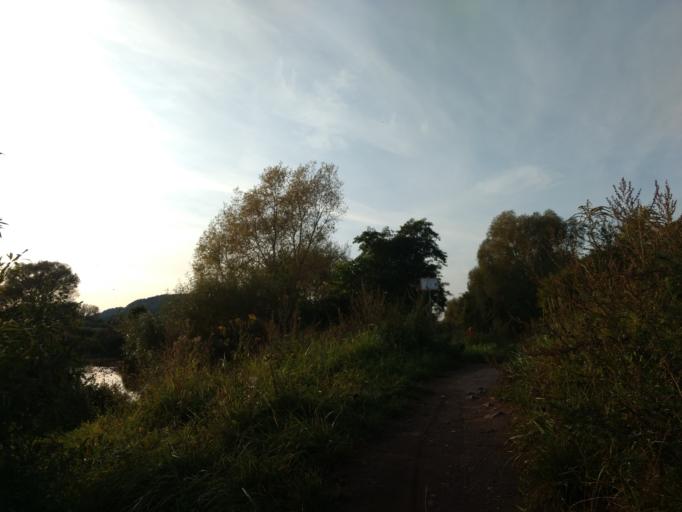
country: DE
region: Saarland
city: Saarlouis
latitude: 49.3286
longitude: 6.7379
